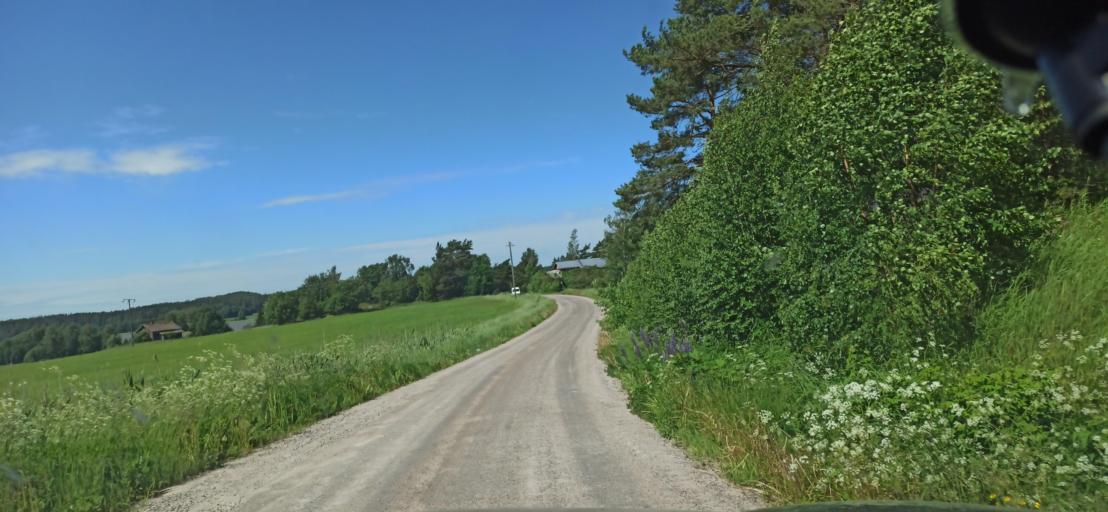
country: FI
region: Varsinais-Suomi
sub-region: Turku
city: Sauvo
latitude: 60.3826
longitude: 22.6361
